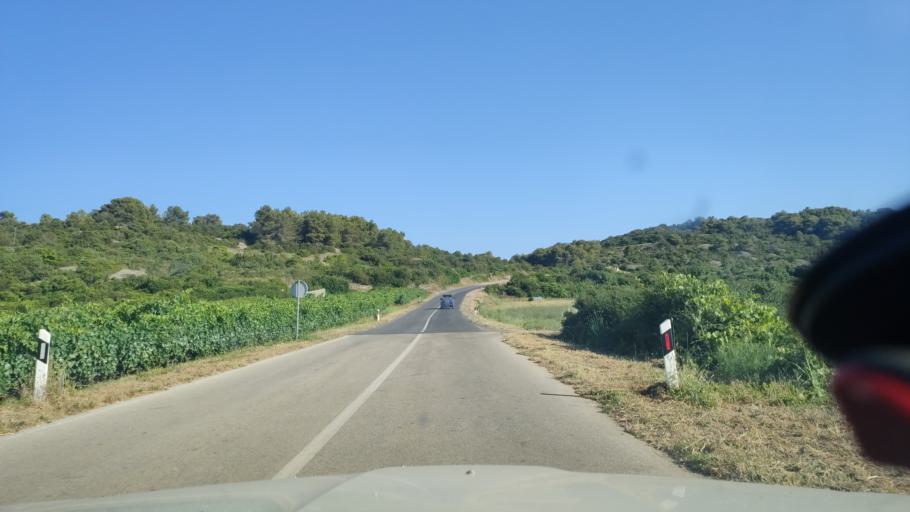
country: HR
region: Splitsko-Dalmatinska
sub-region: Grad Vis
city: Vis
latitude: 43.0404
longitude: 16.1999
